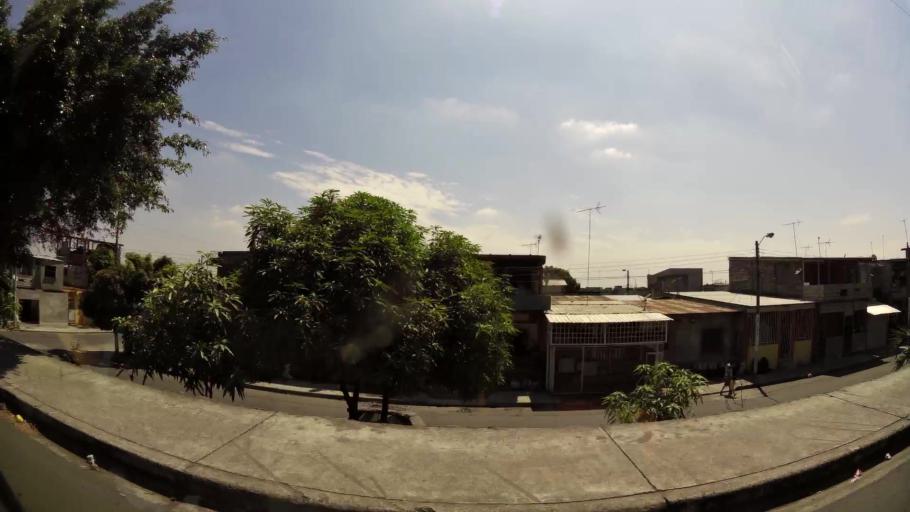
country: EC
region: Guayas
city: Guayaquil
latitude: -2.1258
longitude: -79.9249
